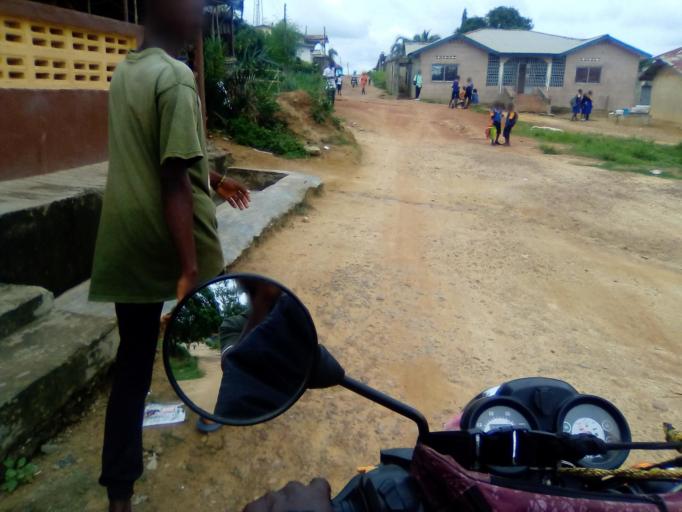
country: SL
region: Southern Province
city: Bo
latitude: 7.9415
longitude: -11.7307
